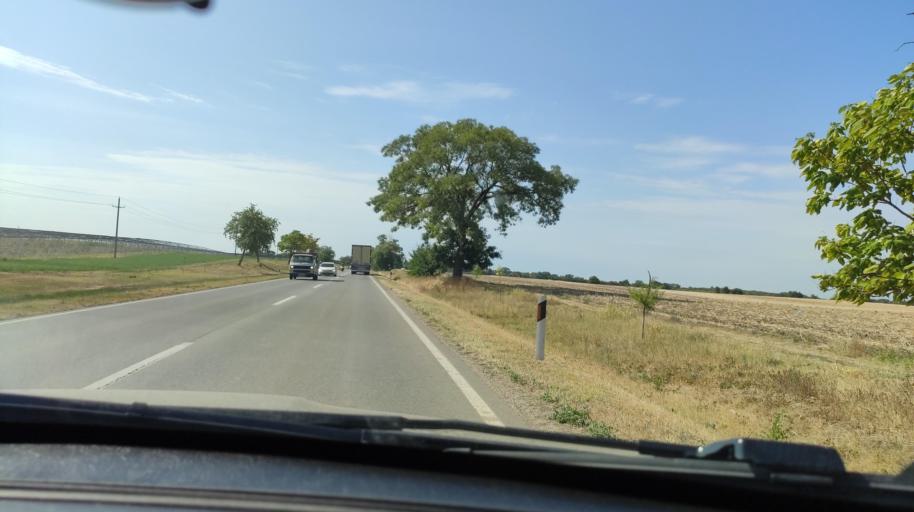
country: RS
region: Autonomna Pokrajina Vojvodina
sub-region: Severnobacki Okrug
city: Backa Topola
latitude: 45.8742
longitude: 19.6346
